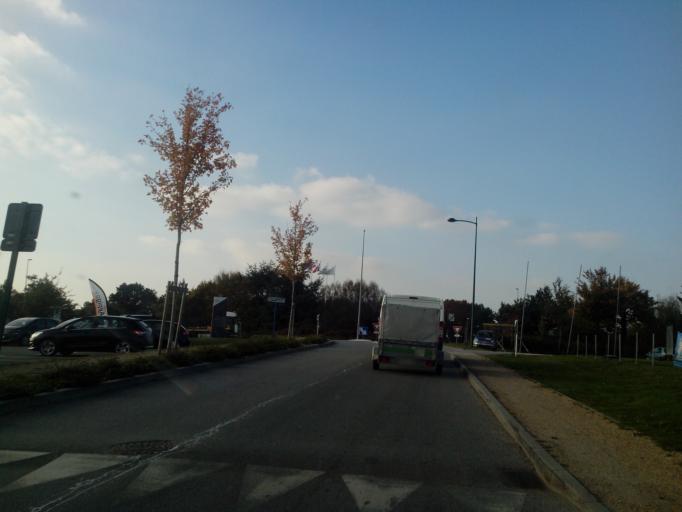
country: FR
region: Brittany
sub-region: Departement du Morbihan
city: Ploermel
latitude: 47.9324
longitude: -2.3799
